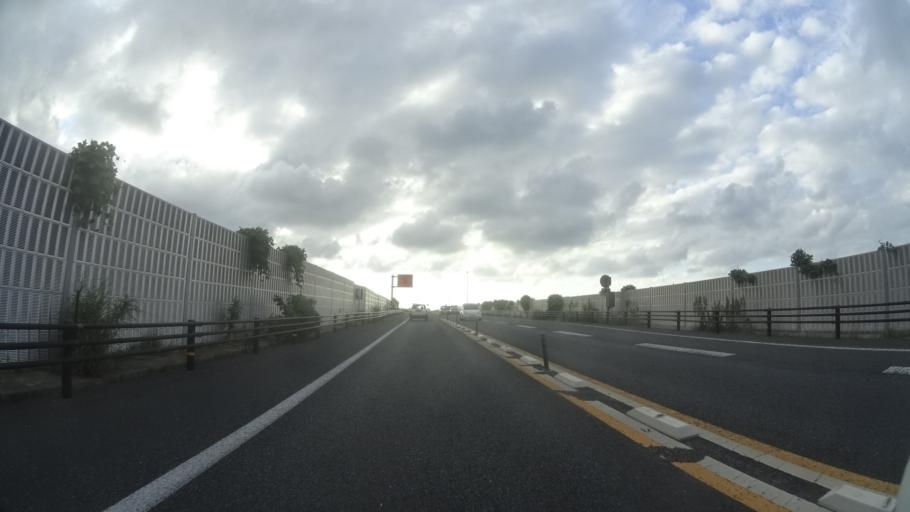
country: JP
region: Tottori
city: Kurayoshi
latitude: 35.5089
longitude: 133.6387
